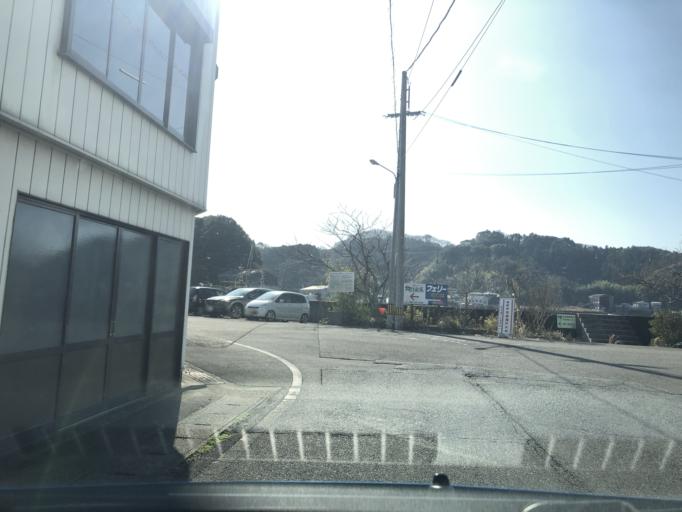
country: JP
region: Kochi
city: Sukumo
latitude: 32.9210
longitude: 132.6993
